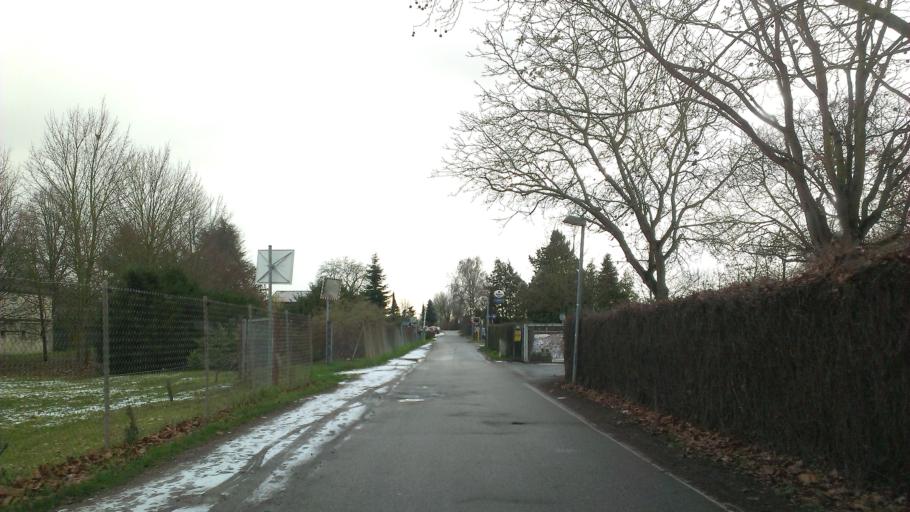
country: DE
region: Rheinland-Pfalz
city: Worms
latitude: 49.6294
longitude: 8.3396
